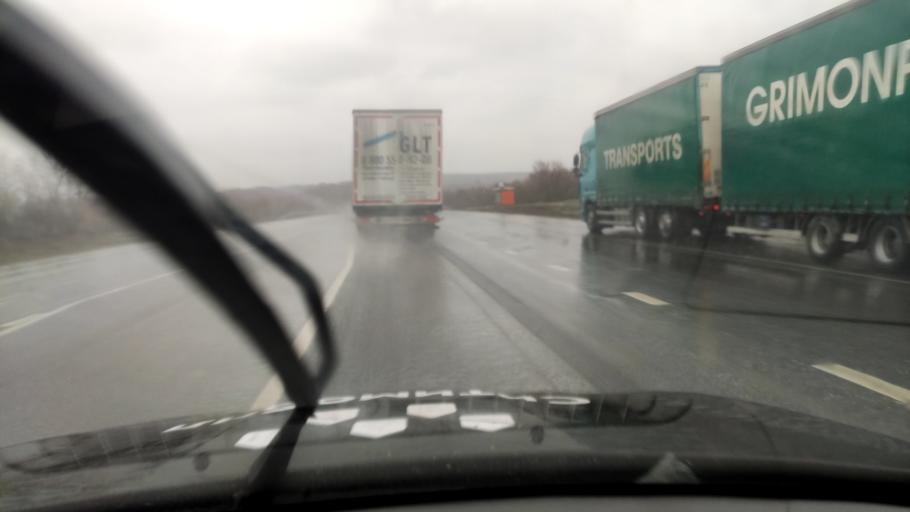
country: RU
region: Samara
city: Mezhdurechensk
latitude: 53.2567
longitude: 49.1262
